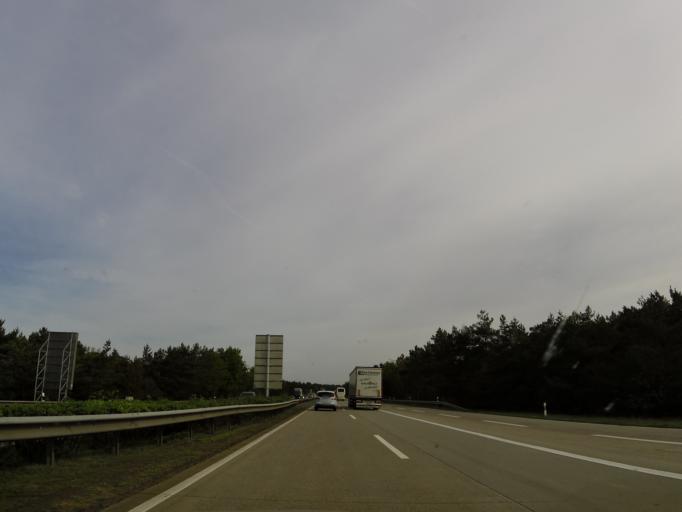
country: DE
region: Lower Saxony
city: Soltau
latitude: 52.9971
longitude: 9.9290
